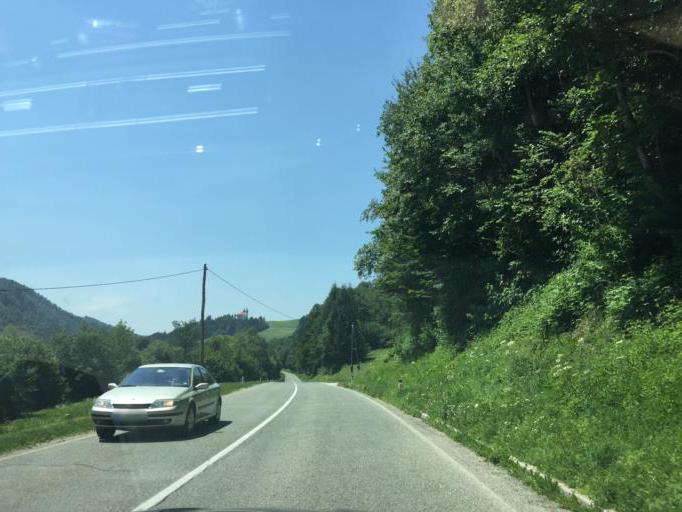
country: SI
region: Skofja Loka
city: Skofja Loka
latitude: 46.1345
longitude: 14.2400
